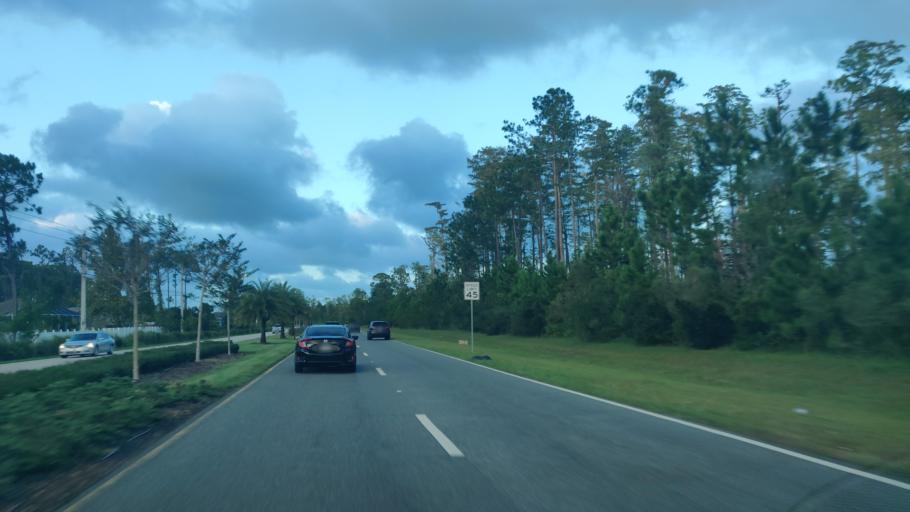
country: US
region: Florida
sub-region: Flagler County
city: Bunnell
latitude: 29.4798
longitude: -81.2208
